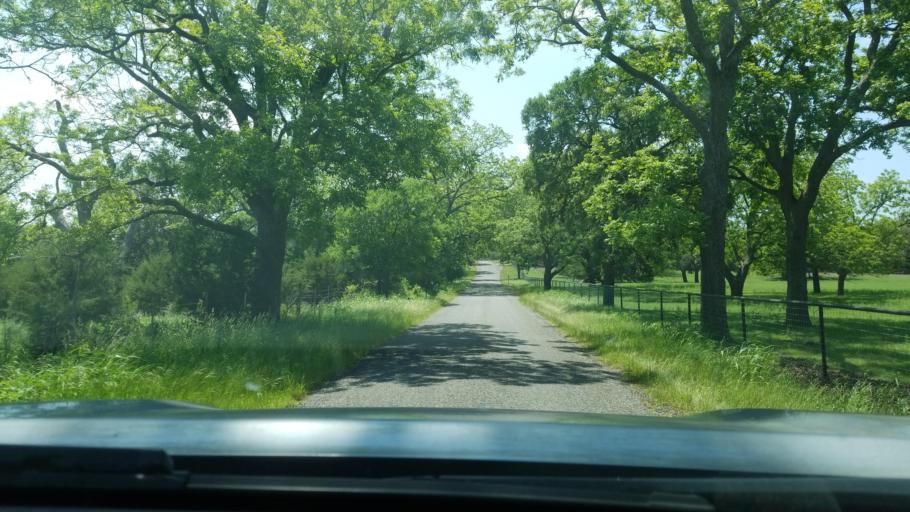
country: US
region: Texas
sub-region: Blanco County
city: Blanco
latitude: 29.9875
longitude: -98.5382
